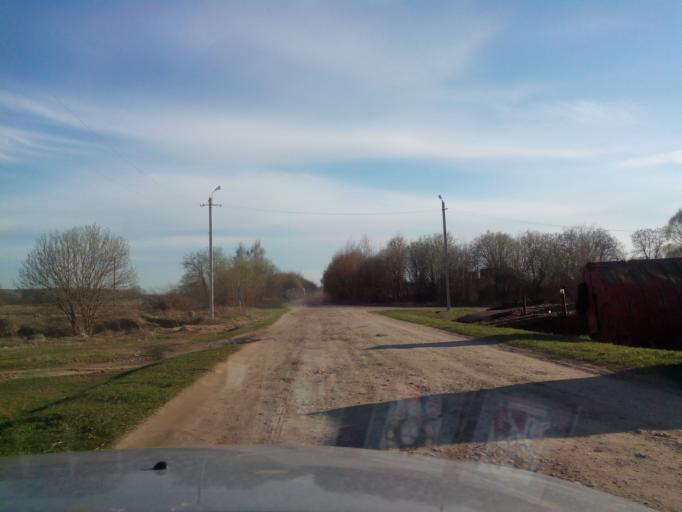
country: RU
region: Rjazan
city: Shilovo
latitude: 54.3832
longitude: 40.8727
